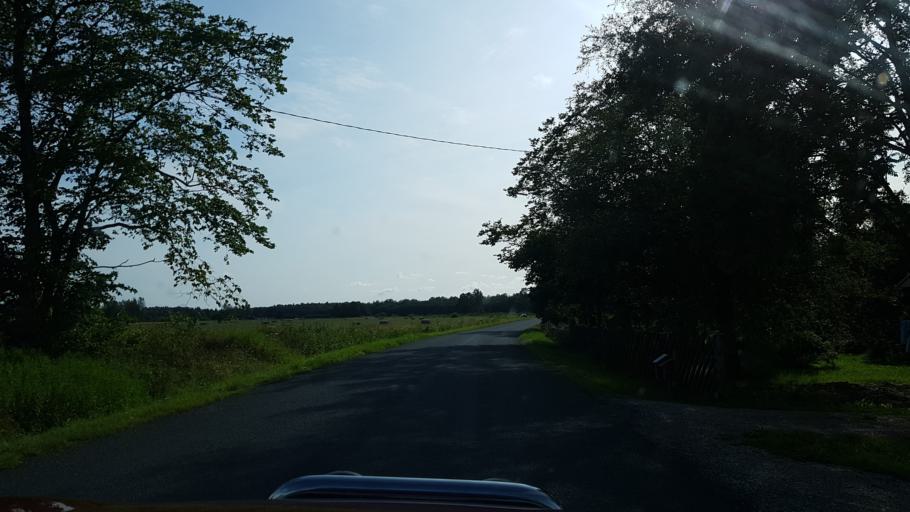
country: EE
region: Laeaene
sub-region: Lihula vald
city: Lihula
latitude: 58.3811
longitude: 24.0043
